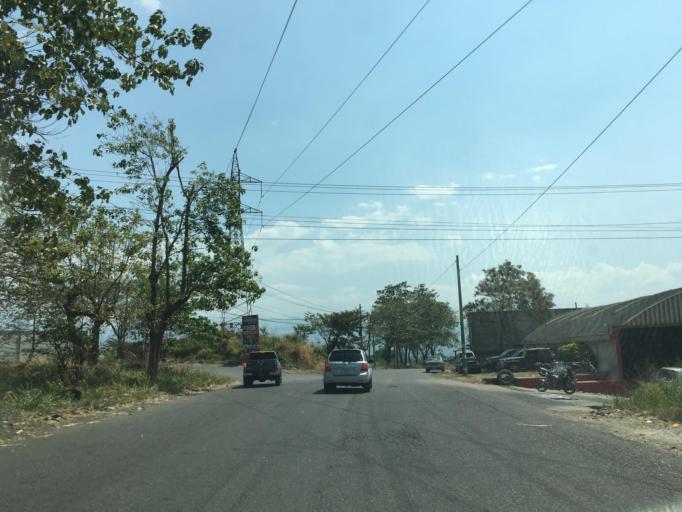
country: GT
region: Escuintla
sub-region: Municipio de Escuintla
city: Escuintla
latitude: 14.2774
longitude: -90.7641
